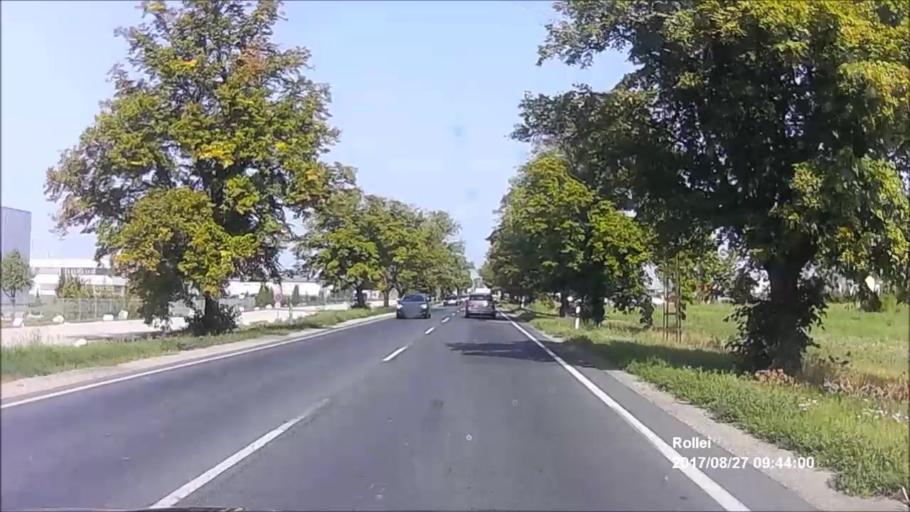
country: HU
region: Gyor-Moson-Sopron
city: Sopron
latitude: 47.6651
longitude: 16.6215
